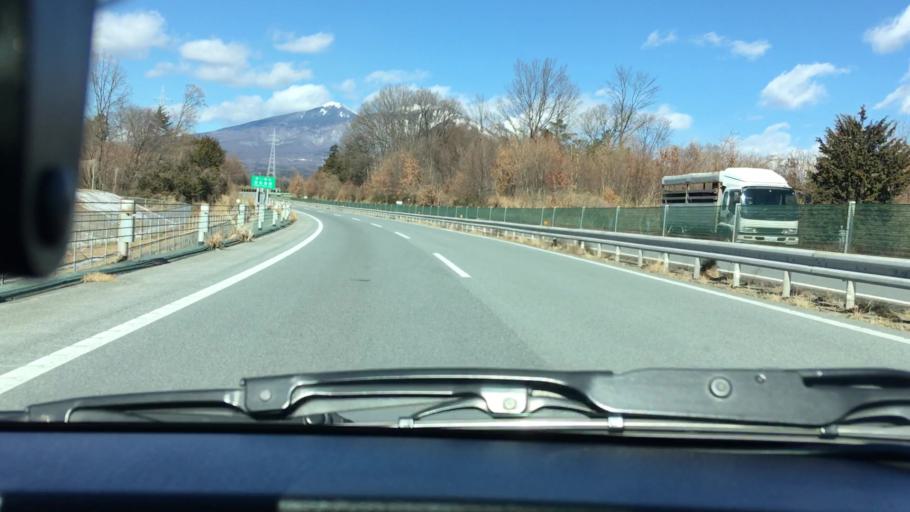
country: JP
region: Yamanashi
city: Nirasaki
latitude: 35.8232
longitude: 138.3944
